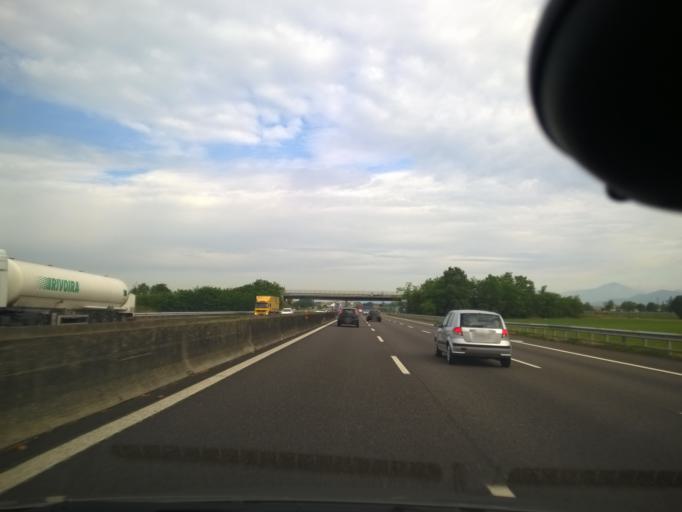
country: IT
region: Lombardy
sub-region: Provincia di Brescia
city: Castegnato
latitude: 45.5438
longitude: 10.1265
